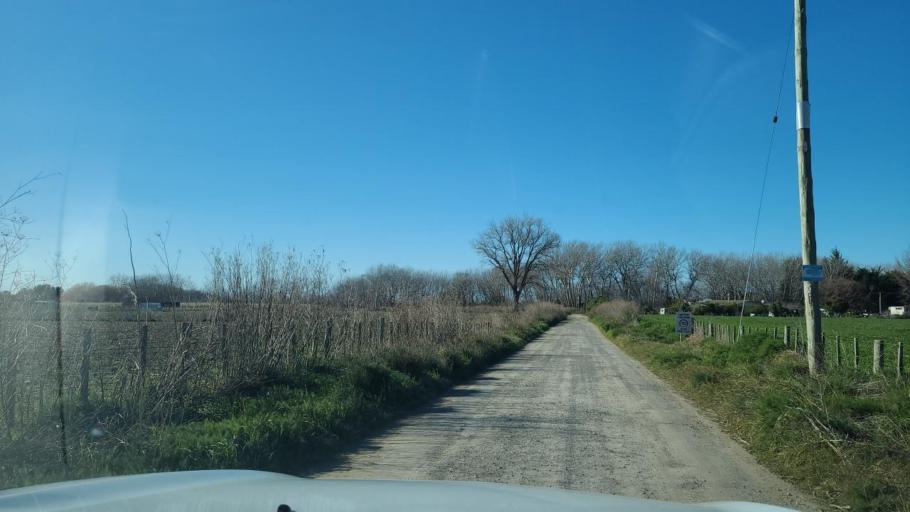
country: NZ
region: Hawke's Bay
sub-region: Hastings District
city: Hastings
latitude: -39.8001
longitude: 176.9838
